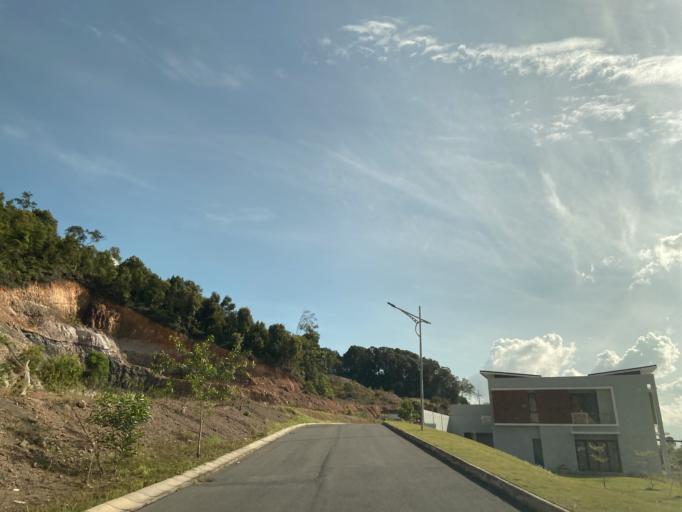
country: SG
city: Singapore
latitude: 1.0960
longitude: 104.0272
